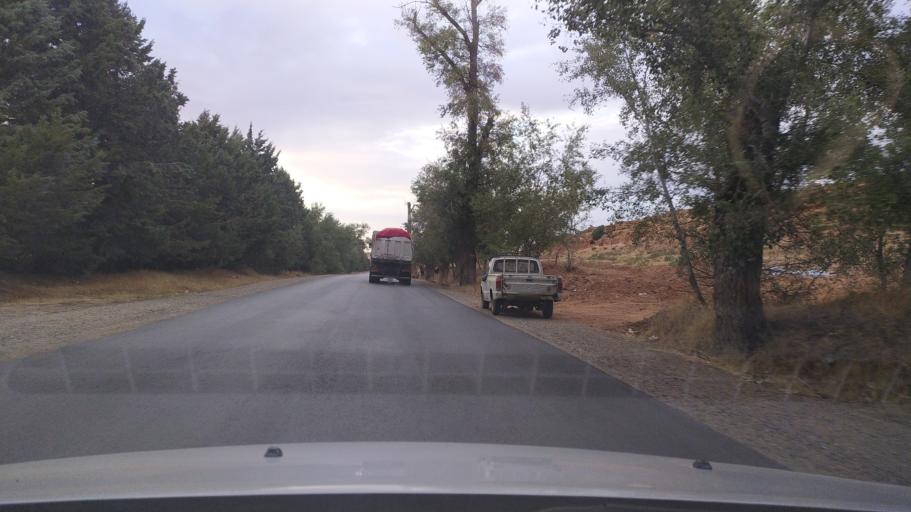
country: DZ
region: Tiaret
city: Frenda
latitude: 35.0486
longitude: 1.0797
